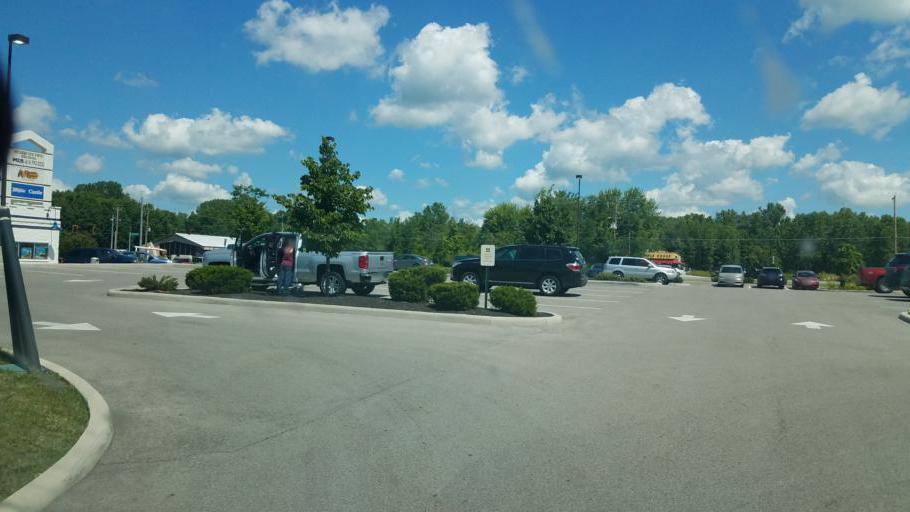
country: US
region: Ohio
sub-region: Delaware County
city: Sunbury
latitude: 40.2660
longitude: -82.9341
